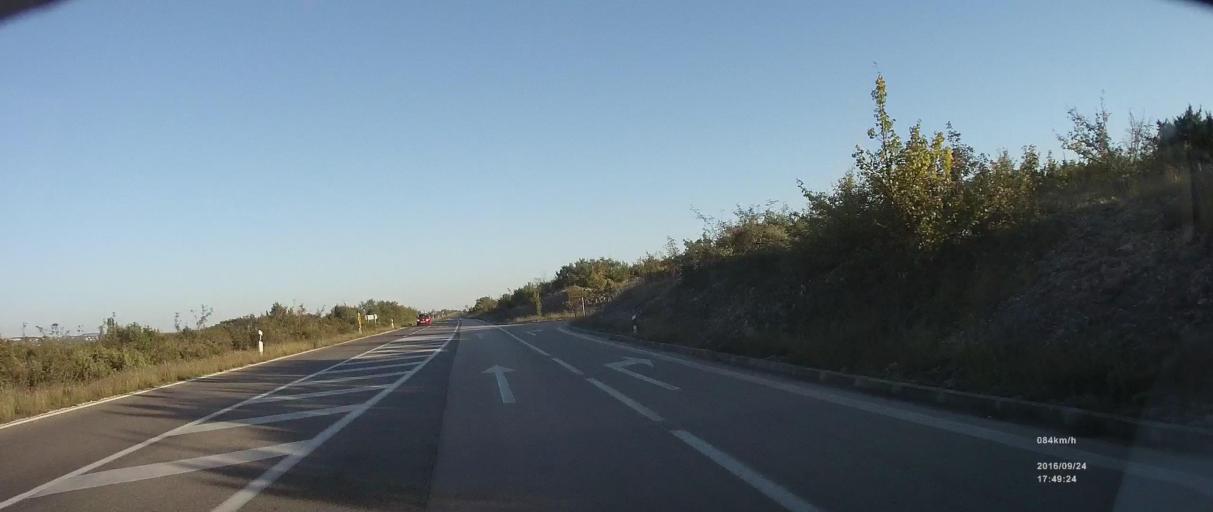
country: HR
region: Zadarska
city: Polaca
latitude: 44.0545
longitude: 15.5493
